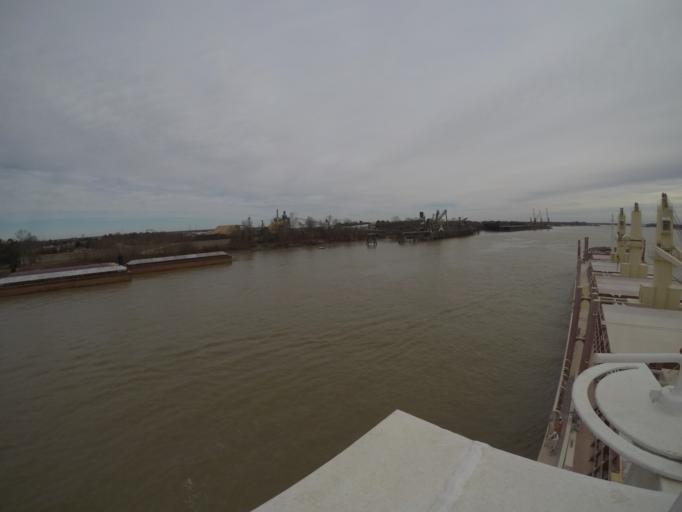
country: US
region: Louisiana
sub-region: Saint John the Baptist Parish
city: Edgard
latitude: 30.0530
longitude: -90.5731
